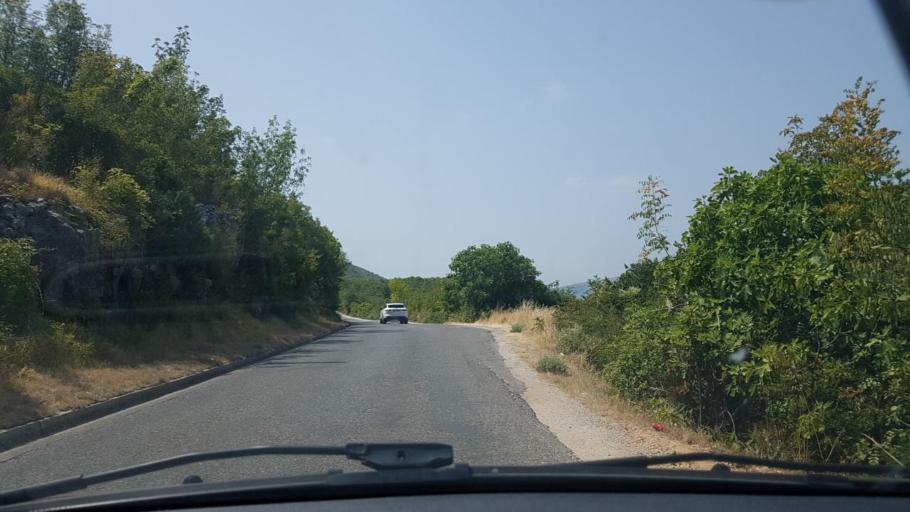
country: HR
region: Dubrovacko-Neretvanska
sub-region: Grad Dubrovnik
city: Metkovic
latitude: 43.0368
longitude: 17.7212
